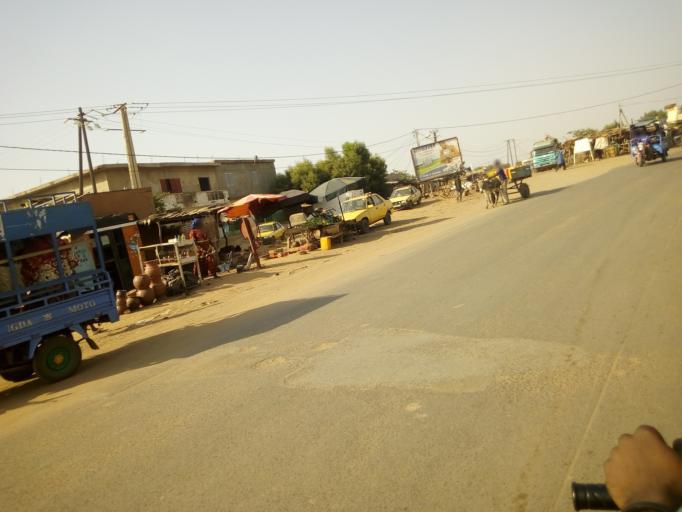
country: ML
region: Kayes
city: Kayes
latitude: 14.4593
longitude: -11.4278
